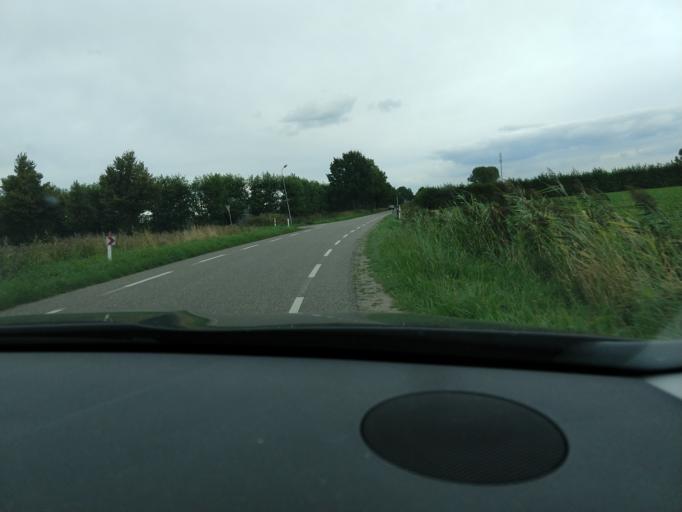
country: NL
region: Zeeland
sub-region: Gemeente Terneuzen
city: Terneuzen
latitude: 51.4093
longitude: 3.8680
